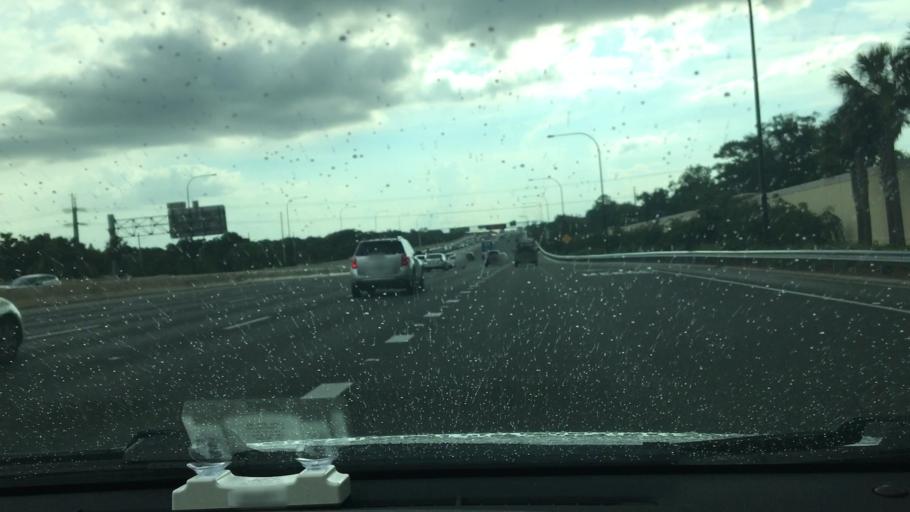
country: US
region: Florida
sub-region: Orange County
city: Azalea Park
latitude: 28.5399
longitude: -81.2925
